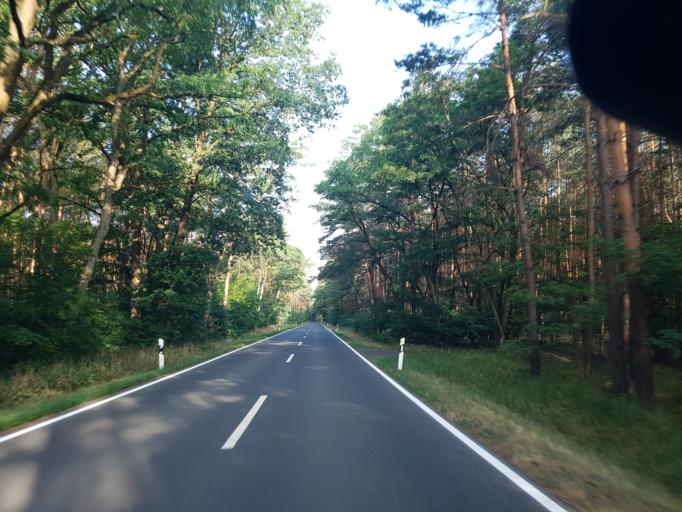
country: DE
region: Saxony-Anhalt
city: Holzdorf
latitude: 51.8497
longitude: 13.1313
